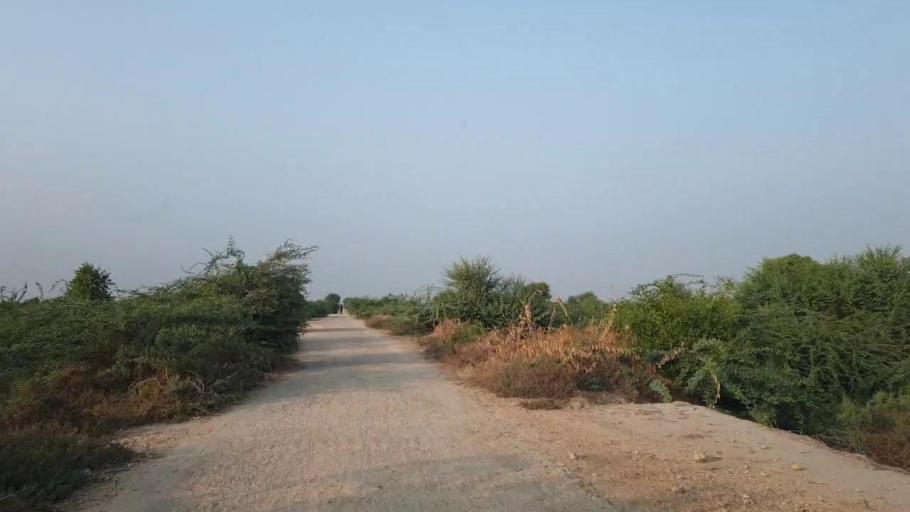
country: PK
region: Sindh
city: Rajo Khanani
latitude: 25.0272
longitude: 68.9772
